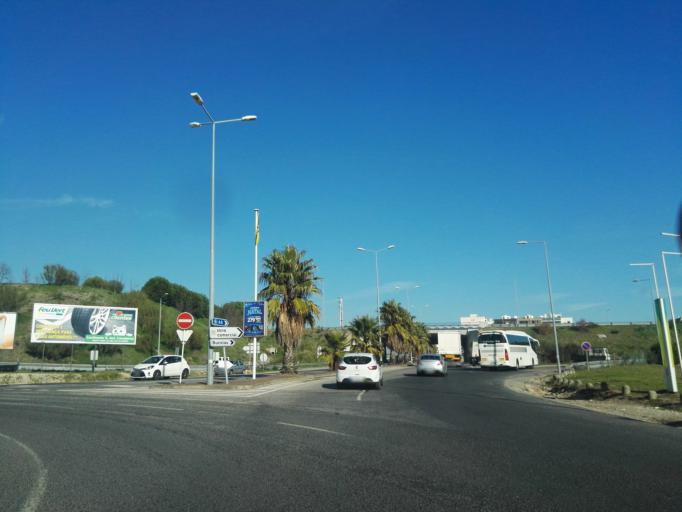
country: PT
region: Lisbon
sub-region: Loures
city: Loures
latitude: 38.8388
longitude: -9.1659
